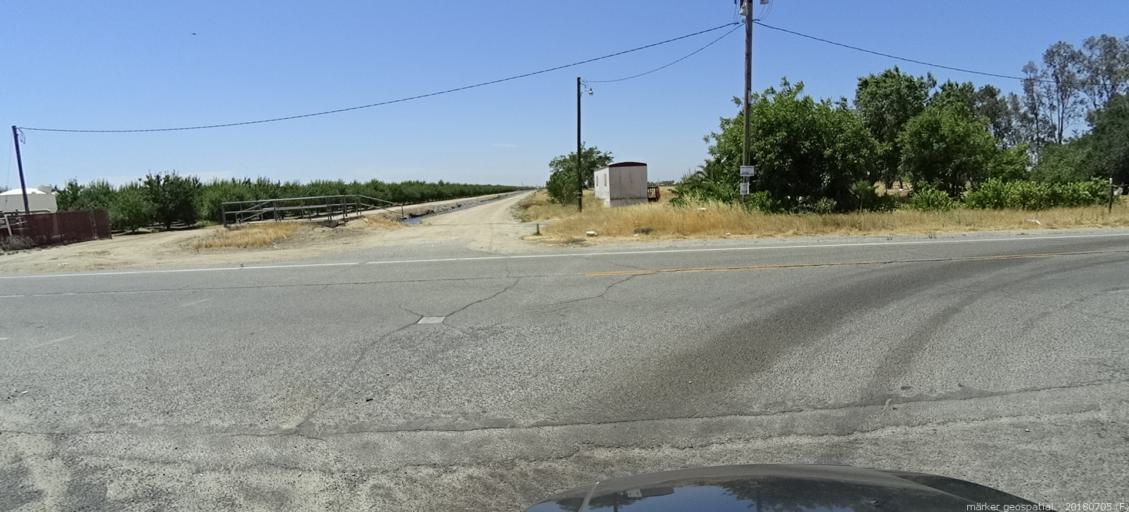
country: US
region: California
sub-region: Madera County
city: Fairmead
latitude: 37.0983
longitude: -120.2022
